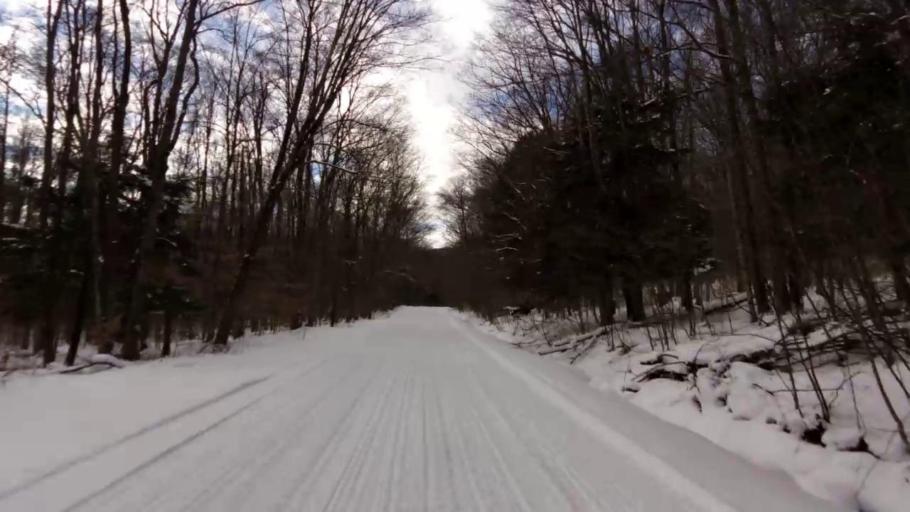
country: US
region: Pennsylvania
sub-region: McKean County
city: Bradford
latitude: 42.0255
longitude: -78.6874
